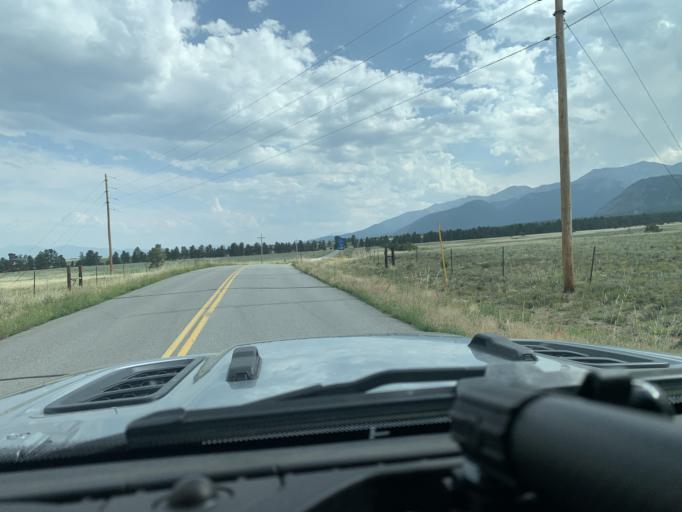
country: US
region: Colorado
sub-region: Chaffee County
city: Buena Vista
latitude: 38.7687
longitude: -106.1464
